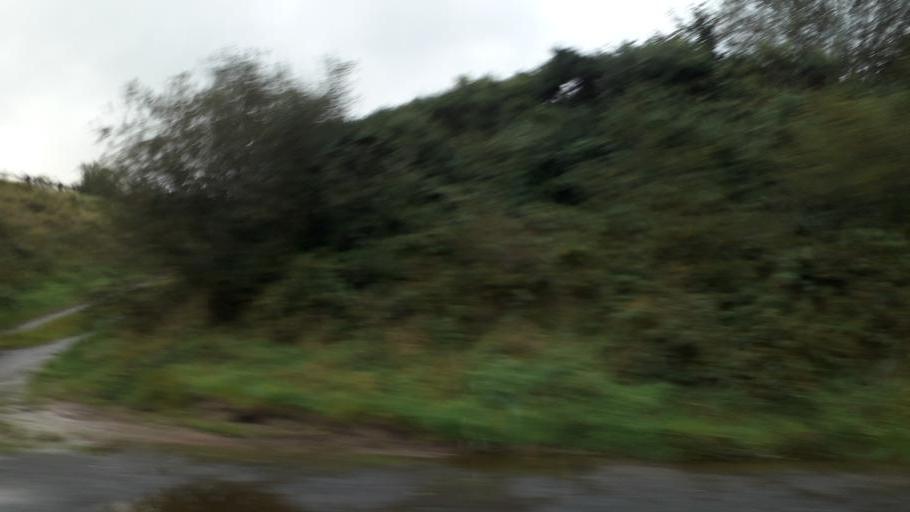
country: IE
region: Leinster
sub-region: An Longfort
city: Lanesborough
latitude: 53.7647
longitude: -8.0401
